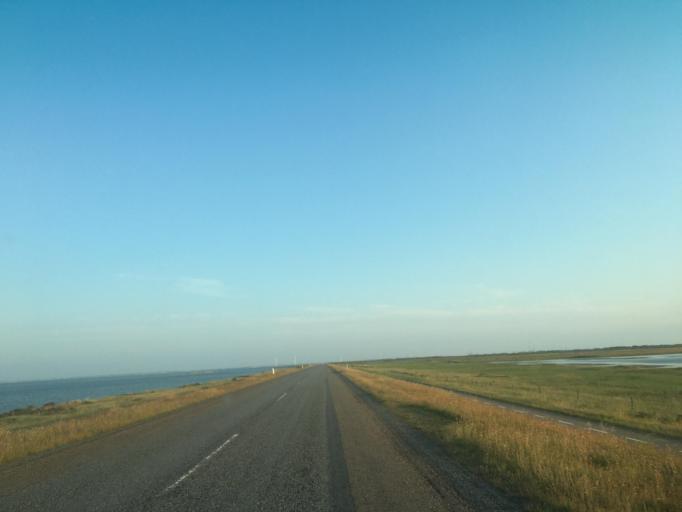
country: DK
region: Central Jutland
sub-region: Lemvig Kommune
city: Thyboron
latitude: 56.7388
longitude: 8.2501
